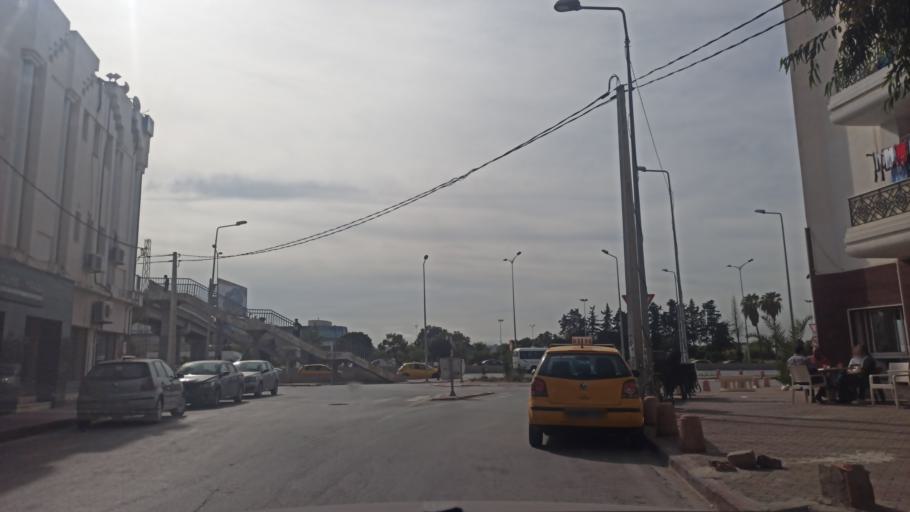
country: TN
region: Tunis
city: La Goulette
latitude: 36.8496
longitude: 10.2635
